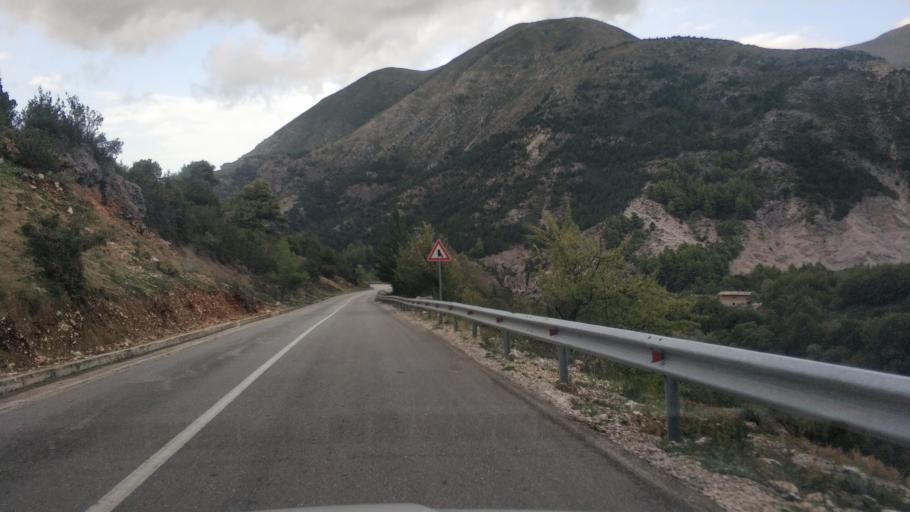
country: AL
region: Vlore
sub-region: Rrethi i Vlores
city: Orikum
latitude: 40.2427
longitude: 19.5511
